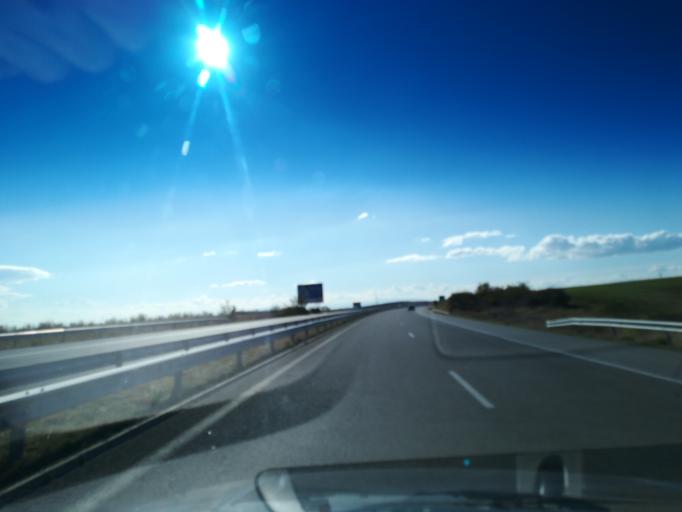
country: BG
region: Stara Zagora
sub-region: Obshtina Chirpan
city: Chirpan
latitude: 42.2551
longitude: 25.4266
